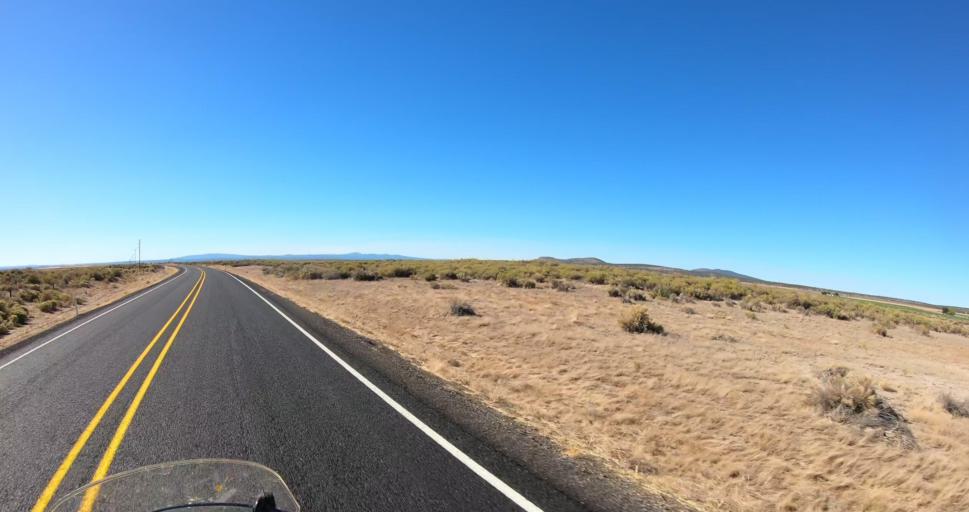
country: US
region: Oregon
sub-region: Deschutes County
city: La Pine
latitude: 43.1309
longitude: -120.9049
